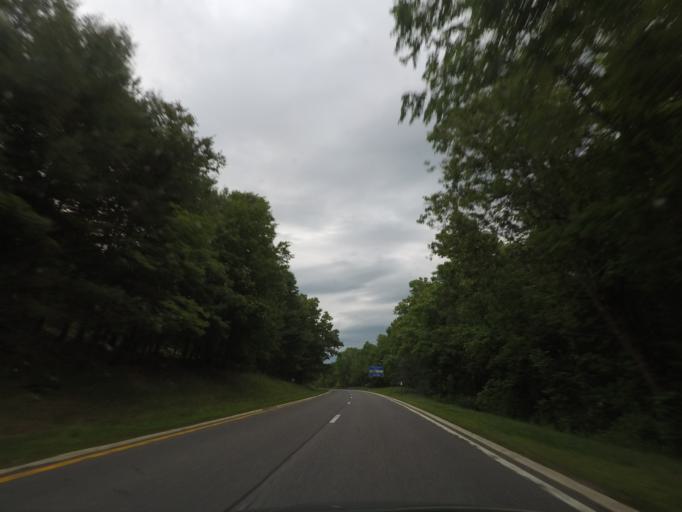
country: US
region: New York
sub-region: Dutchess County
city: Pine Plains
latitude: 42.0196
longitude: -73.7333
